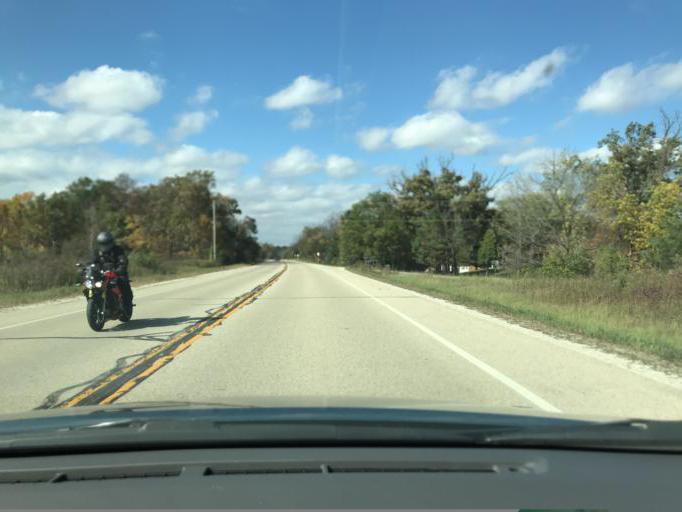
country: US
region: Wisconsin
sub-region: Racine County
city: Browns Lake
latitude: 42.6398
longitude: -88.1809
